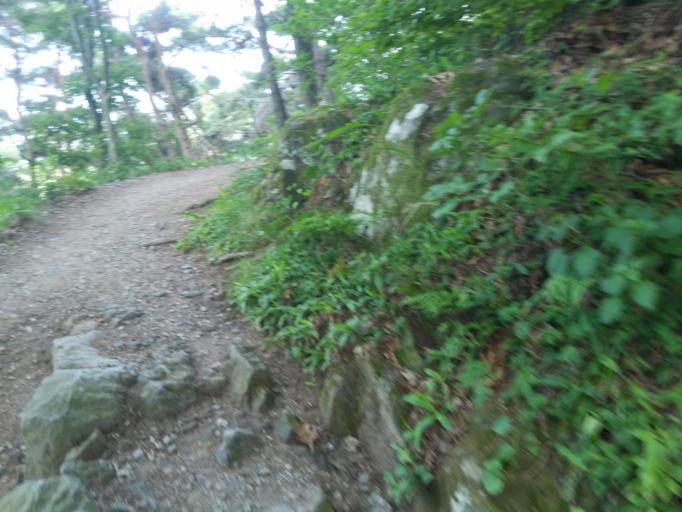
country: KR
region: Daegu
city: Hwawon
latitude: 35.7858
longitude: 128.5466
